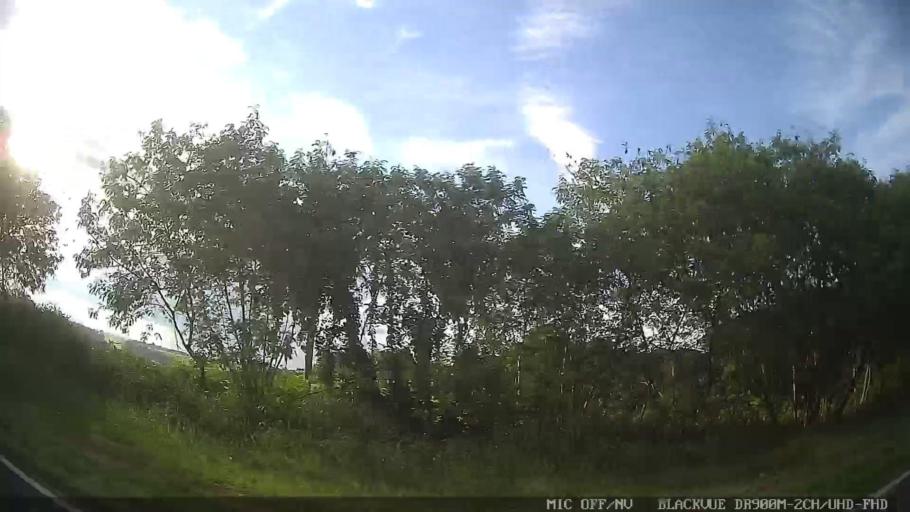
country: BR
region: Sao Paulo
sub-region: Tiete
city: Tiete
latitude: -23.0878
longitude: -47.7197
